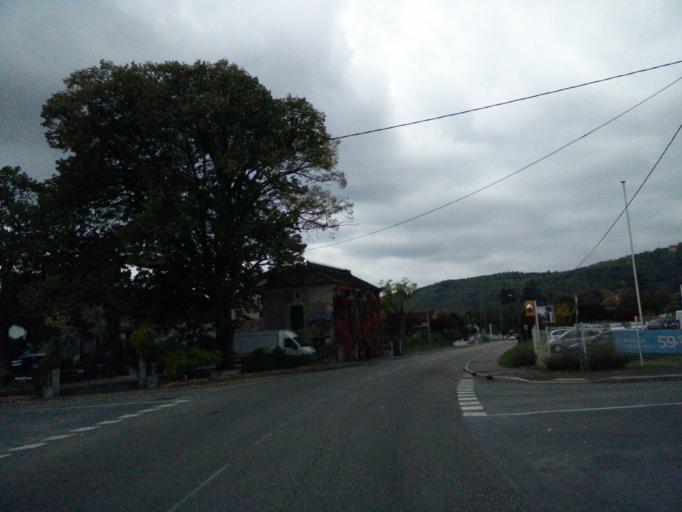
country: FR
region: Midi-Pyrenees
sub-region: Departement du Lot
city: Prayssac
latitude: 44.5034
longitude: 1.1798
